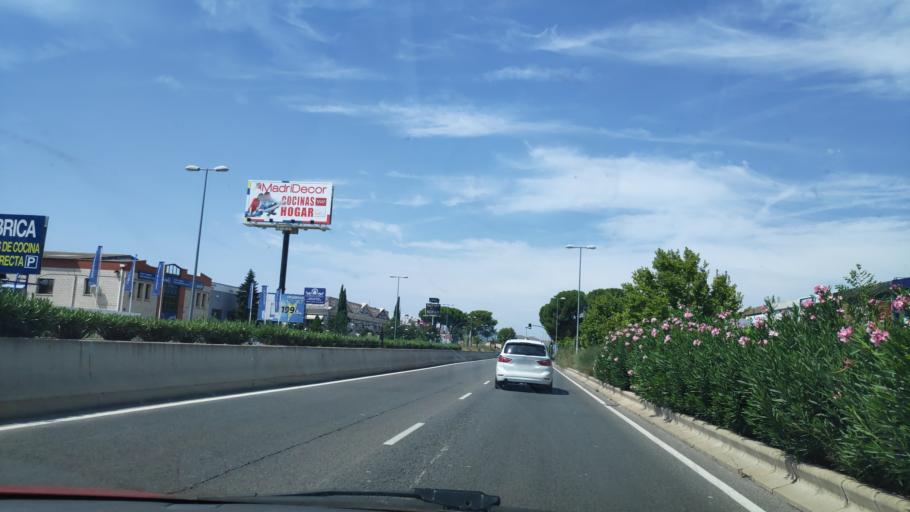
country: ES
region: Madrid
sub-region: Provincia de Madrid
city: Vaciamadrid
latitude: 40.3107
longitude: -3.4828
